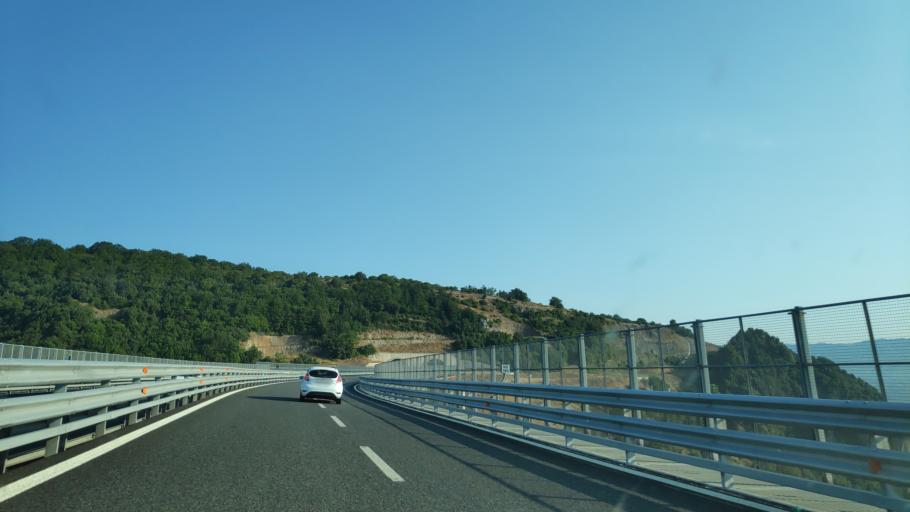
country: IT
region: Calabria
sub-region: Provincia di Cosenza
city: Laino Castello-Nuovo Centro
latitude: 39.9397
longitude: 15.9593
